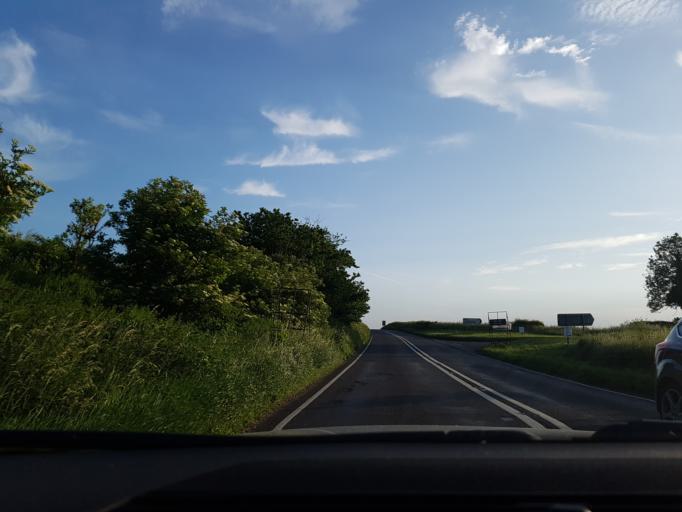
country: GB
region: England
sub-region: Northamptonshire
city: Deanshanger
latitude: 52.0203
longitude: -0.9291
